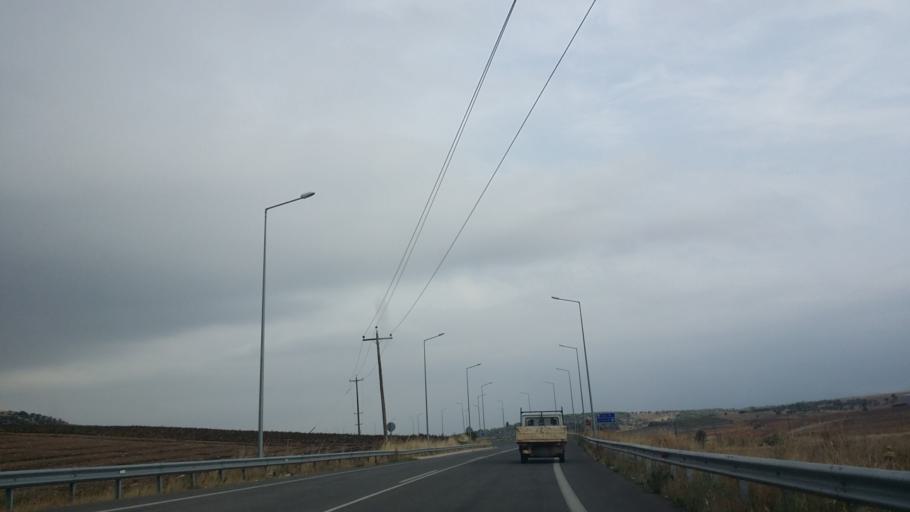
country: GR
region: Central Greece
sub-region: Nomos Voiotias
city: Thespies
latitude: 38.2969
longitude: 23.1635
